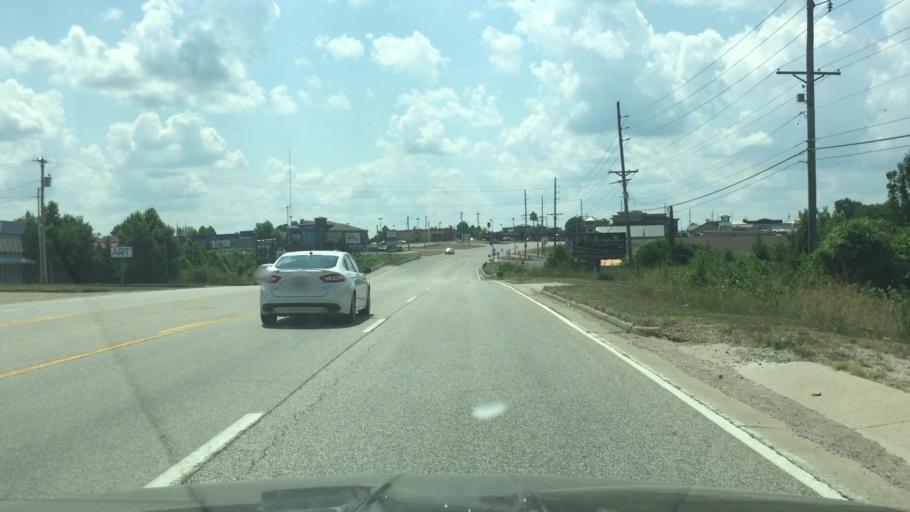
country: US
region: Missouri
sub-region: Miller County
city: Lake Ozark
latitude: 38.1726
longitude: -92.6138
